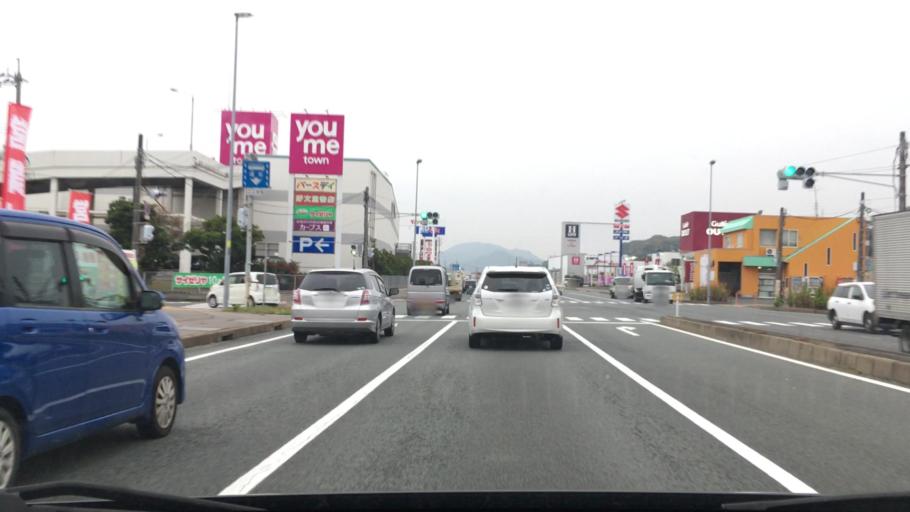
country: JP
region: Yamaguchi
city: Shimonoseki
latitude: 34.0316
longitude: 131.0132
